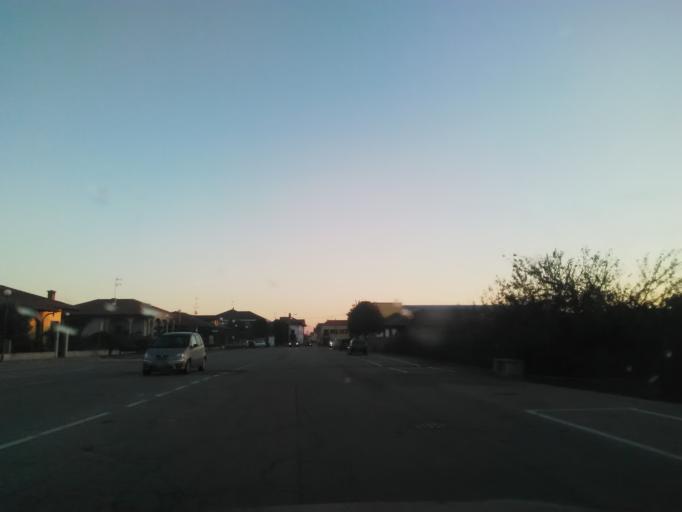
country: IT
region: Piedmont
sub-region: Provincia di Vercelli
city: Tronzano Vercellese
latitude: 45.3433
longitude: 8.1715
